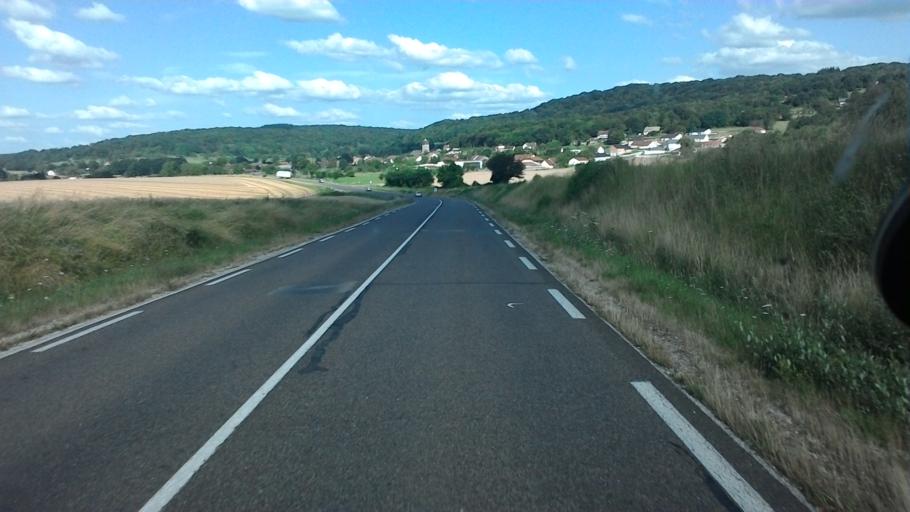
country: FR
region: Franche-Comte
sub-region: Departement de la Haute-Saone
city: Rioz
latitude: 47.5350
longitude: 6.0358
